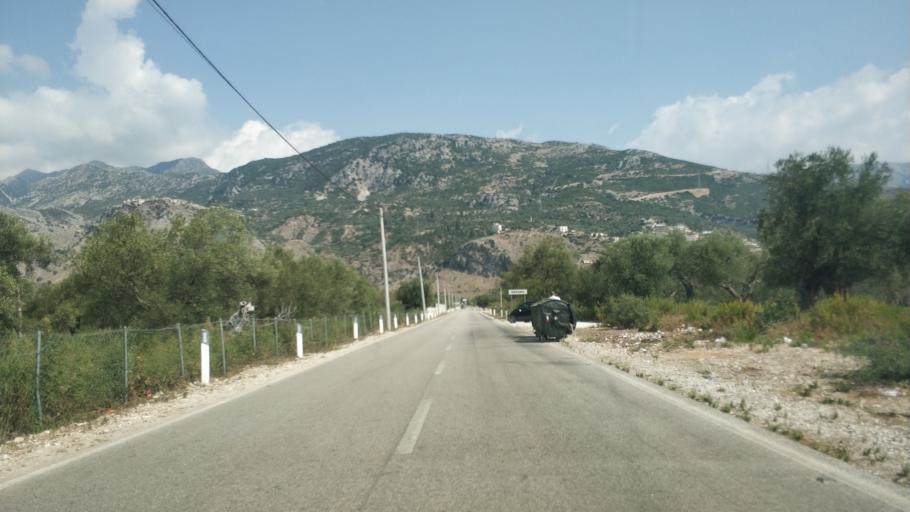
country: AL
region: Vlore
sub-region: Rrethi i Vlores
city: Himare
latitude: 40.0546
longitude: 19.8147
